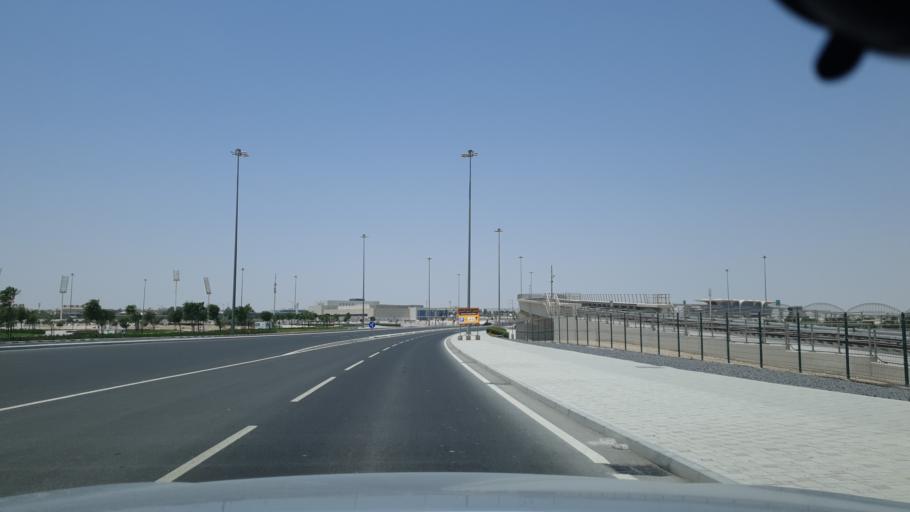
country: QA
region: Baladiyat ad Dawhah
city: Doha
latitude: 25.3773
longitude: 51.5030
